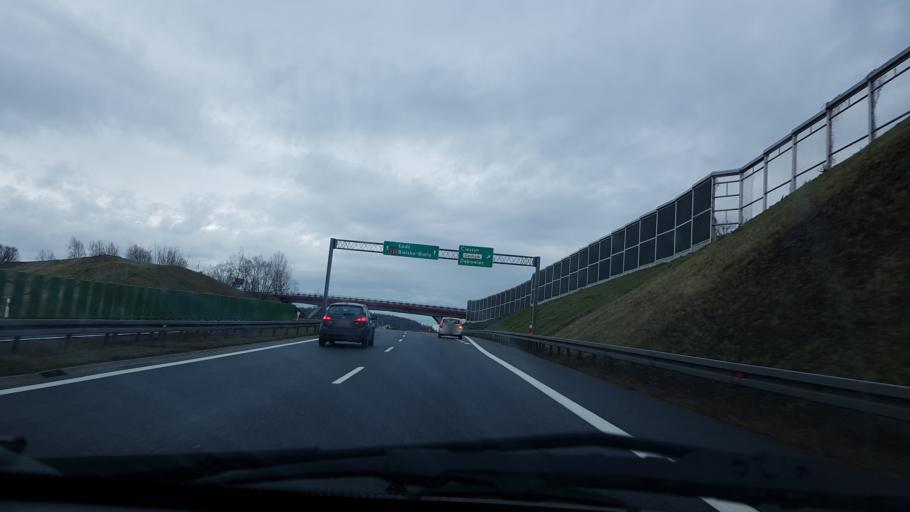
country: PL
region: Silesian Voivodeship
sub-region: Powiat cieszynski
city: Zamarski
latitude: 49.7627
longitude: 18.6797
